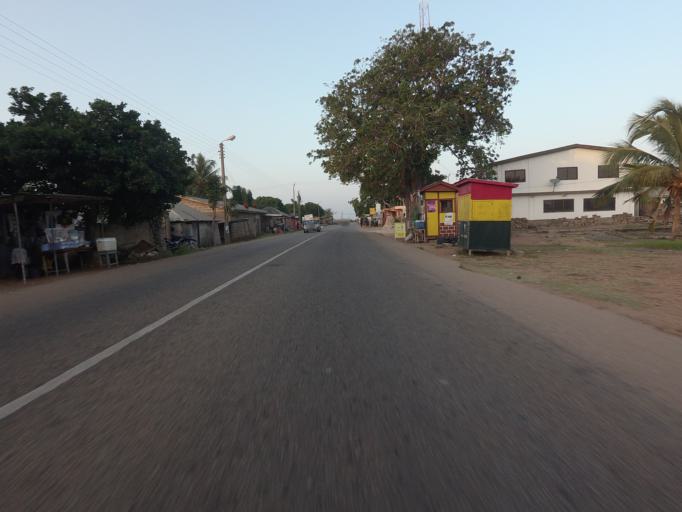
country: GH
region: Volta
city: Anloga
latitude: 5.7961
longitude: 0.9044
